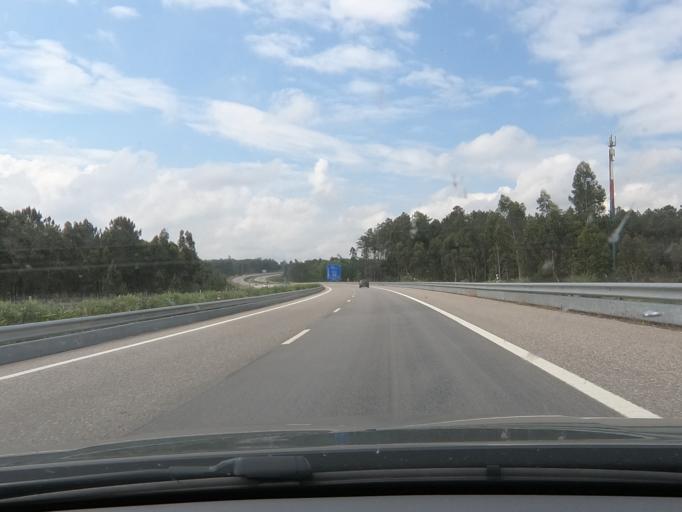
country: PT
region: Leiria
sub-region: Leiria
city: Amor
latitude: 39.7611
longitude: -8.8755
